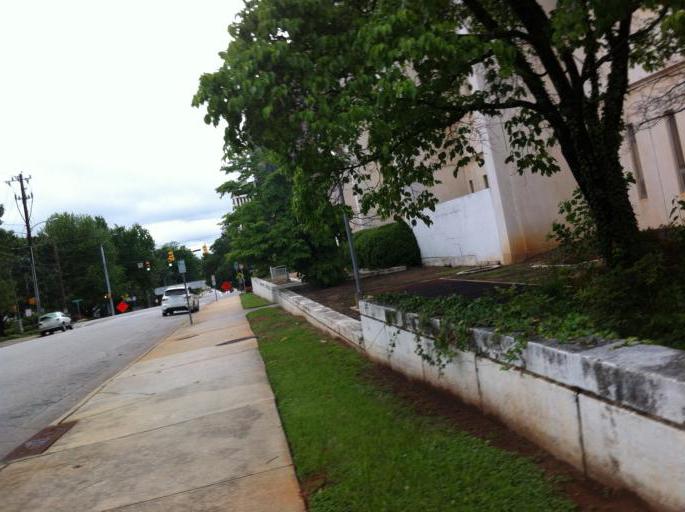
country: US
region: North Carolina
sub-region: Wake County
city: Raleigh
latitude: 35.7839
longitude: -78.6371
